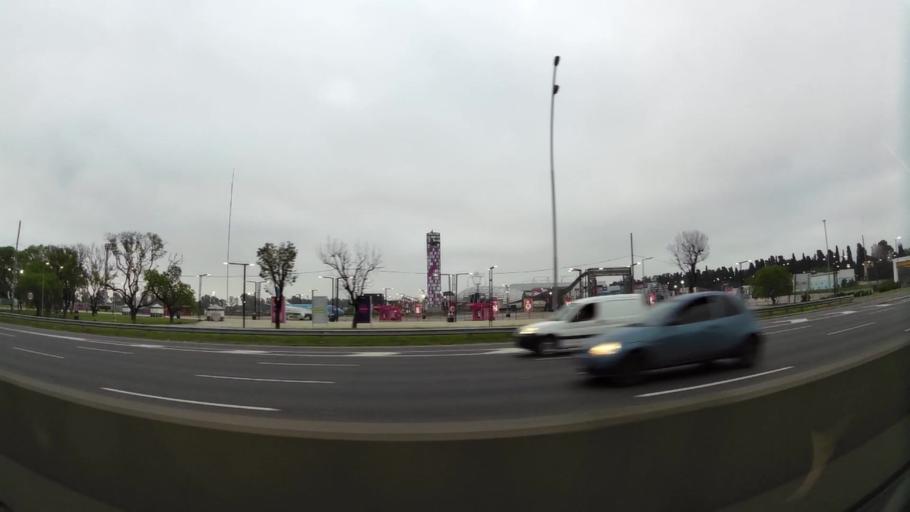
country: AR
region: Buenos Aires
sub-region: Partido de General San Martin
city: General San Martin
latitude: -34.5608
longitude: -58.5053
